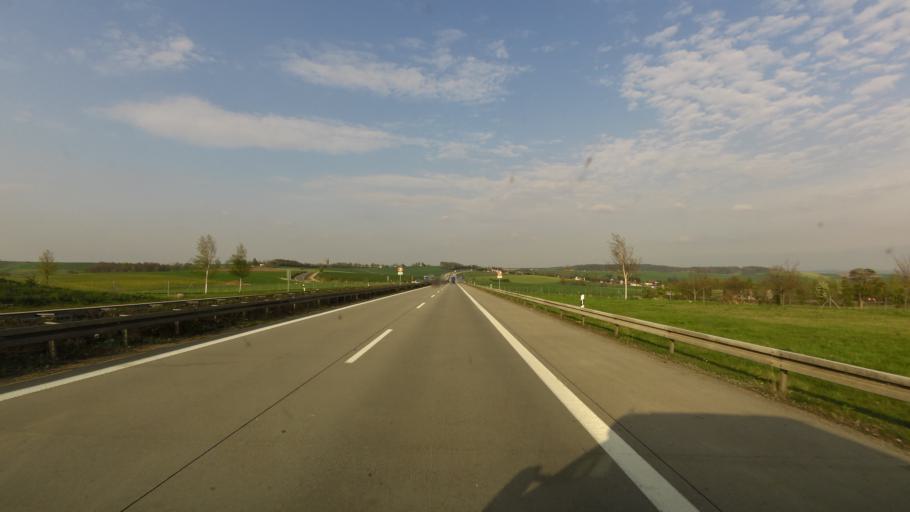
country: DE
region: Saxony
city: Reinsdorf
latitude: 50.6826
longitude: 12.5865
